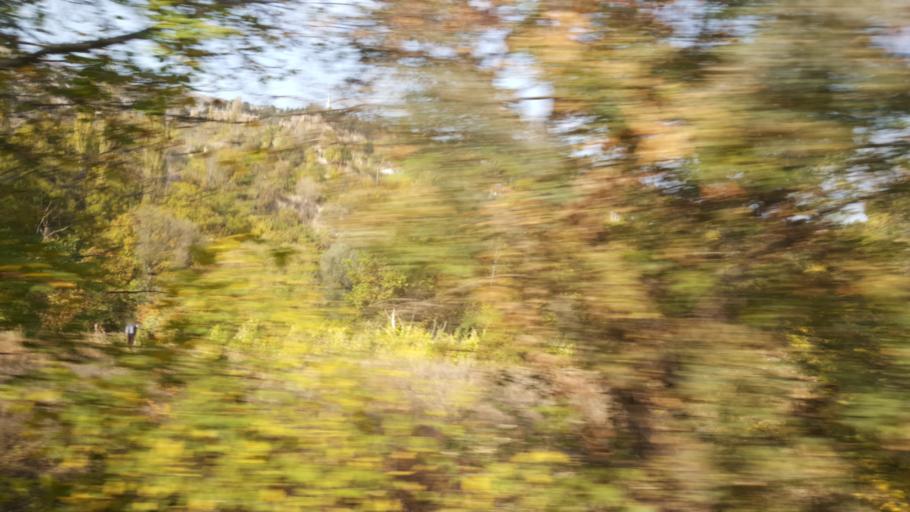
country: TR
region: Eskisehir
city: Mihaliccik
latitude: 39.9870
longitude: 31.3435
